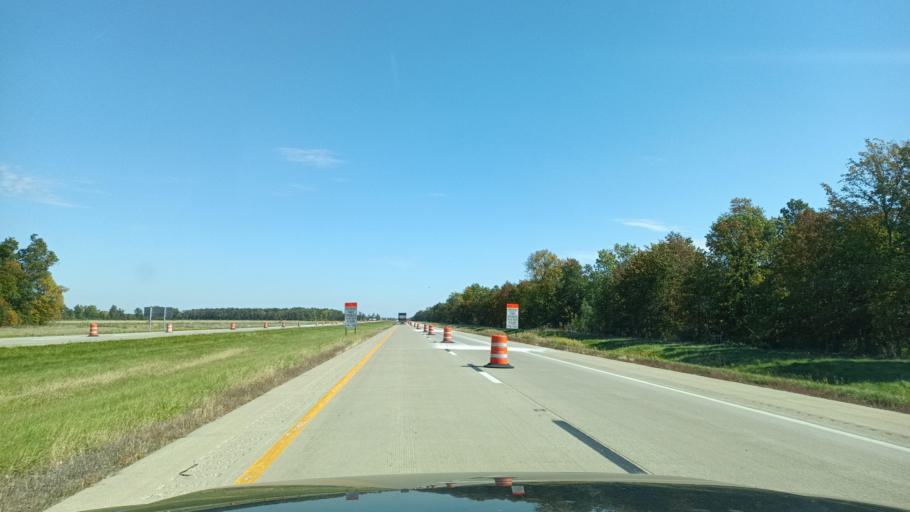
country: US
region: Ohio
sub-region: Paulding County
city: Paulding
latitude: 41.2431
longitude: -84.5078
